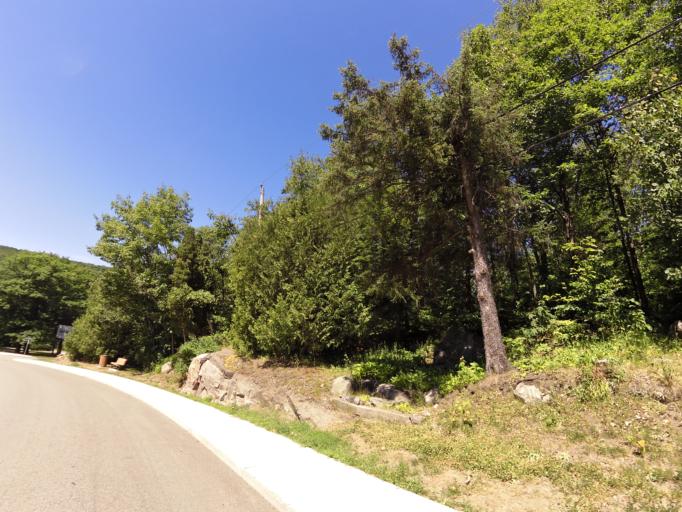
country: CA
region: Quebec
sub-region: Abitibi-Temiscamingue
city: Temiscaming
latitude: 46.7184
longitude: -79.1018
